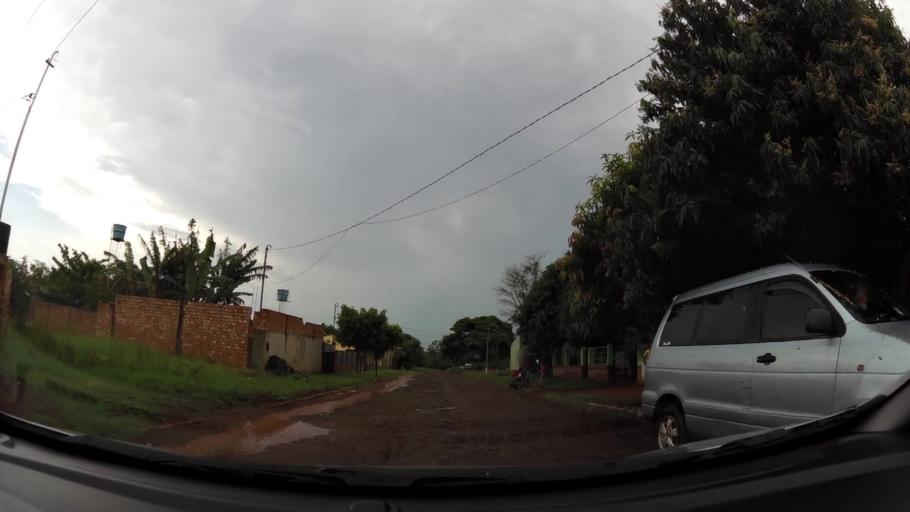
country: PY
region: Alto Parana
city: Presidente Franco
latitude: -25.5442
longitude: -54.6488
